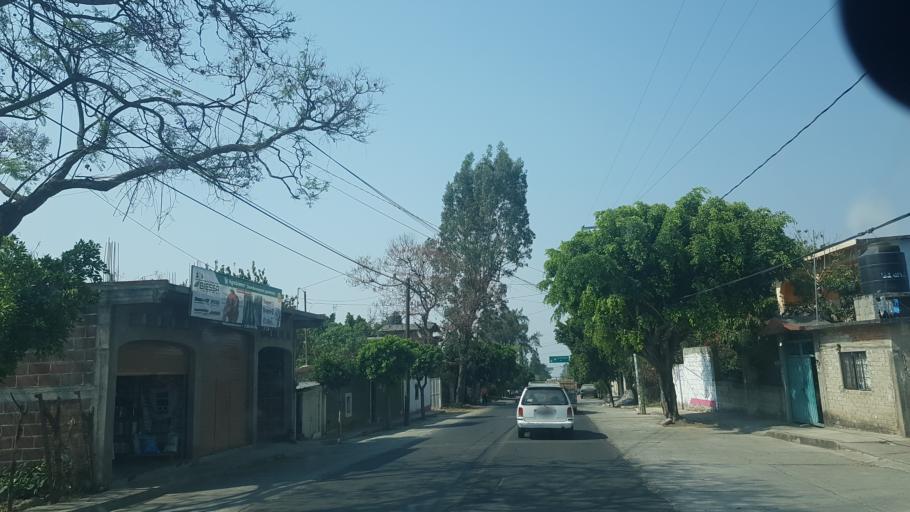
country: MX
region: Morelos
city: Tlacotepec
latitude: 18.8089
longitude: -98.7588
